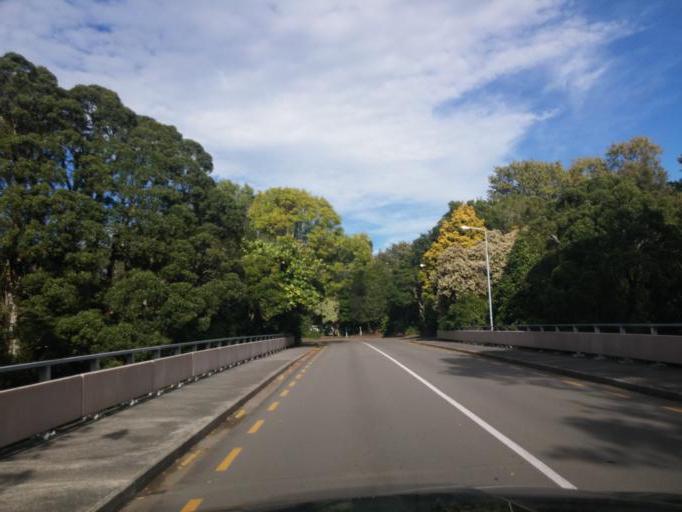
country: NZ
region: Manawatu-Wanganui
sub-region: Palmerston North City
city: Palmerston North
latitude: -40.3853
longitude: 175.6152
